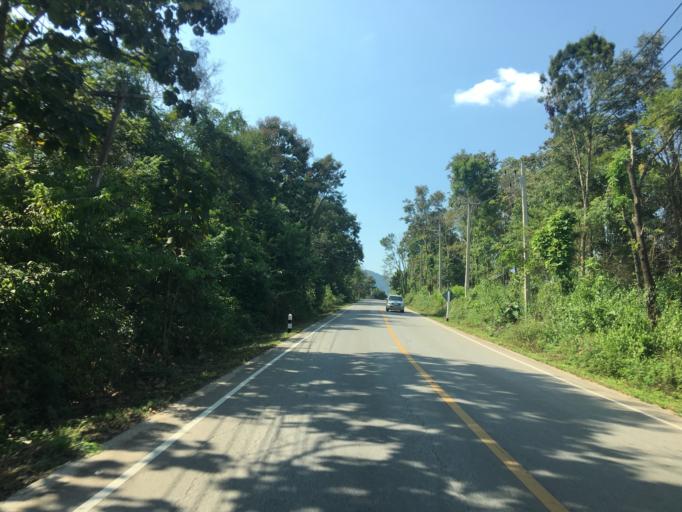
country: TH
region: Nan
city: Ban Luang
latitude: 18.8444
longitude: 100.4056
